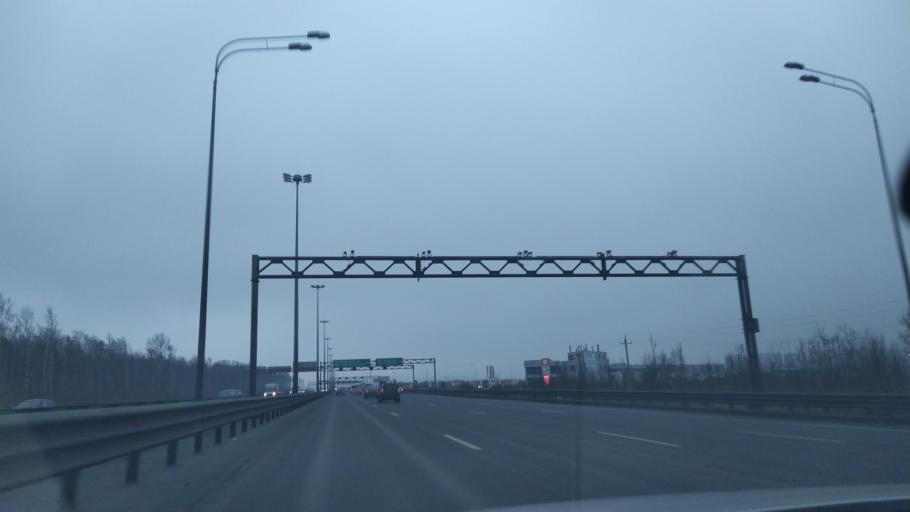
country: RU
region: Leningrad
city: Rybatskoye
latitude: 59.8829
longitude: 30.5268
